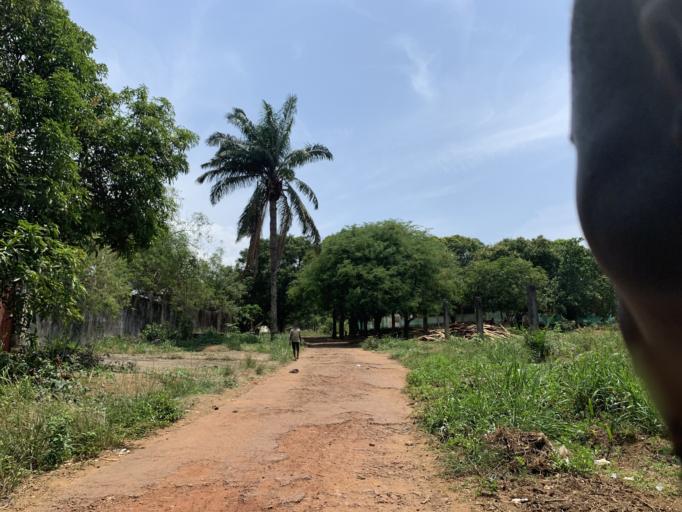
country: SL
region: Western Area
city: Waterloo
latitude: 8.3367
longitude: -13.0350
